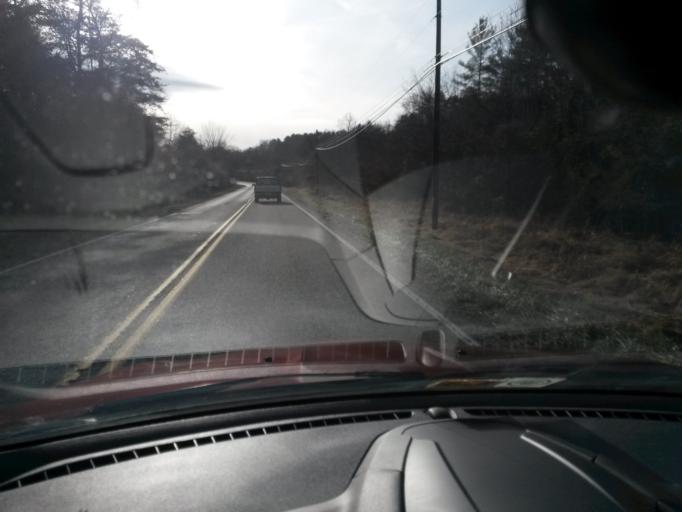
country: US
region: Virginia
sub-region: Rockbridge County
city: East Lexington
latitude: 38.0704
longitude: -79.4009
